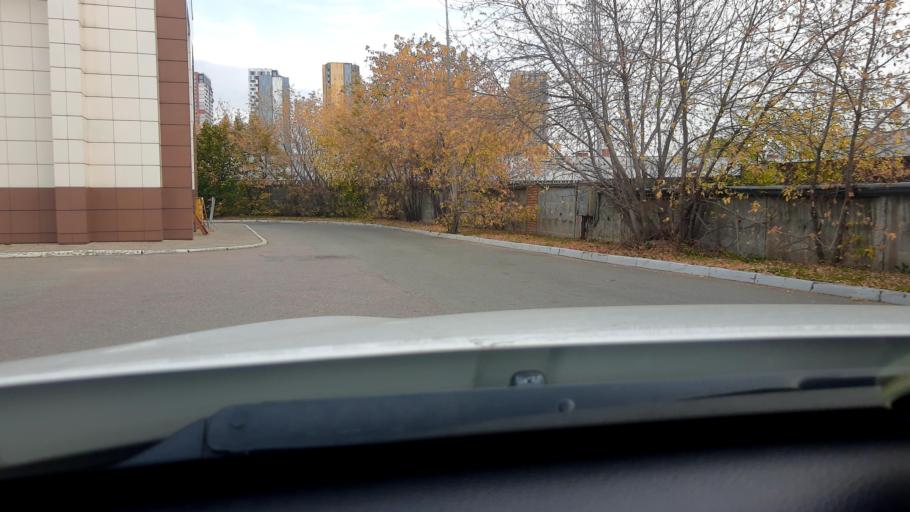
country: RU
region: Moskovskaya
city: Bogorodskoye
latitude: 55.8070
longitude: 37.7405
